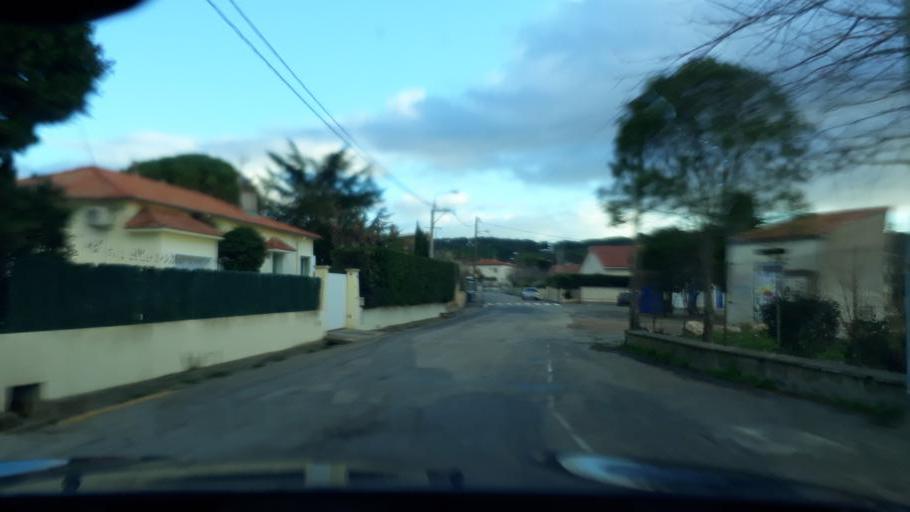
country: FR
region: Languedoc-Roussillon
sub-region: Departement de l'Herault
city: Nissan-lez-Enserune
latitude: 43.2877
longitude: 3.1312
